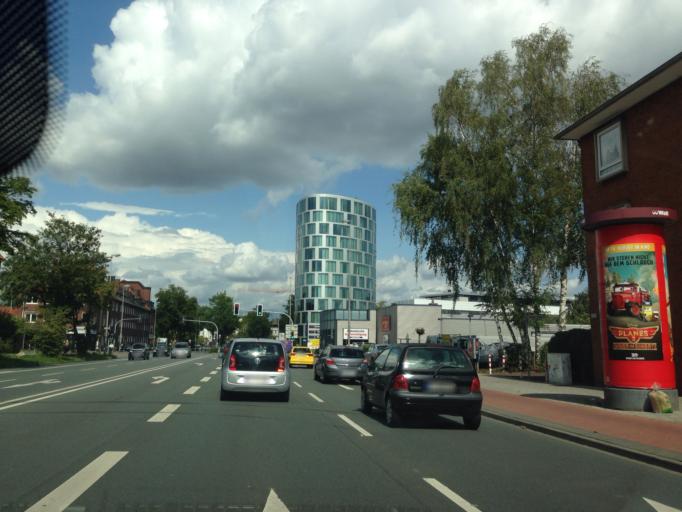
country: DE
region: North Rhine-Westphalia
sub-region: Regierungsbezirk Munster
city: Muenster
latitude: 51.9400
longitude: 7.6244
